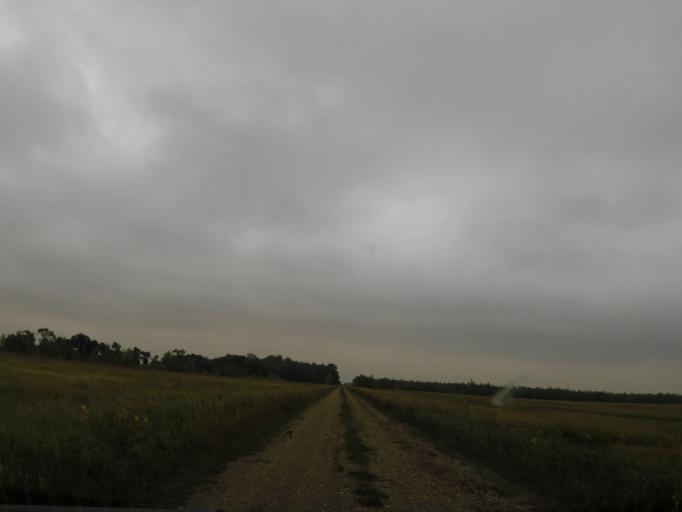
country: US
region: North Dakota
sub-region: Walsh County
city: Grafton
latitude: 48.4277
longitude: -97.1253
